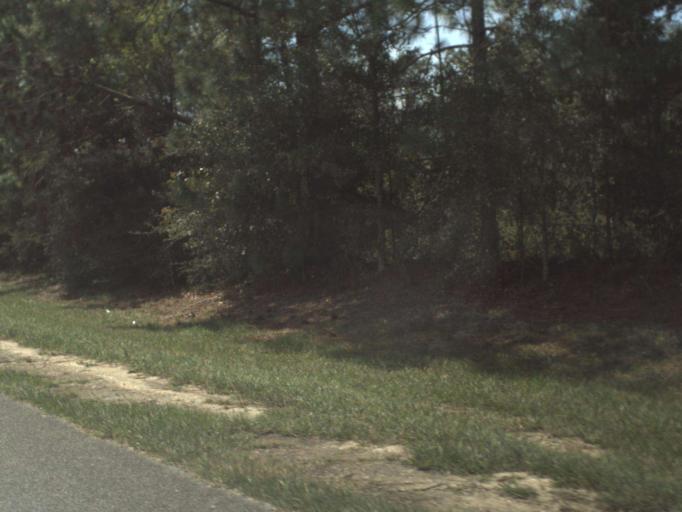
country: US
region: Florida
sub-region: Washington County
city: Chipley
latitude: 30.7195
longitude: -85.5550
